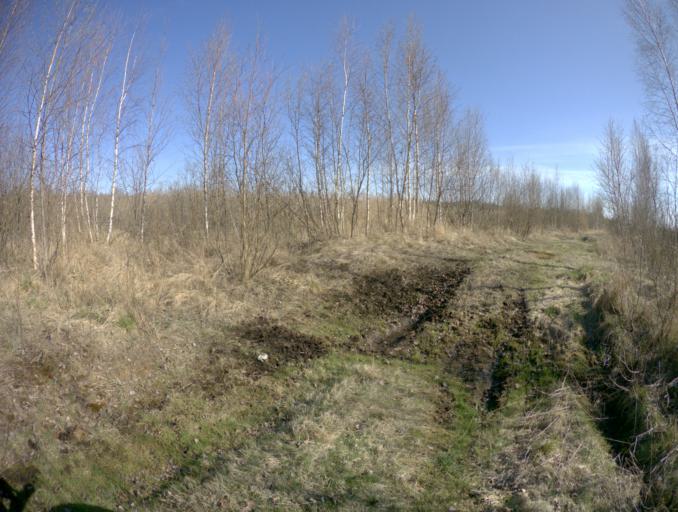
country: RU
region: Vladimir
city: Ivanishchi
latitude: 55.7175
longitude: 40.4315
